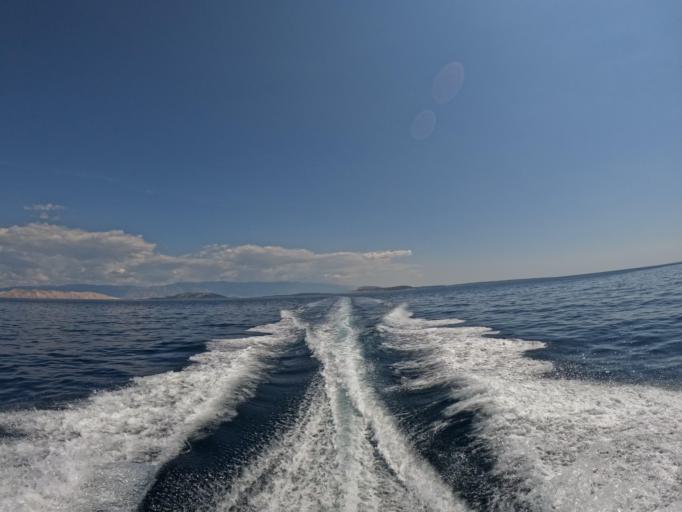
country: HR
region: Primorsko-Goranska
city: Lopar
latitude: 44.8903
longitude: 14.6340
